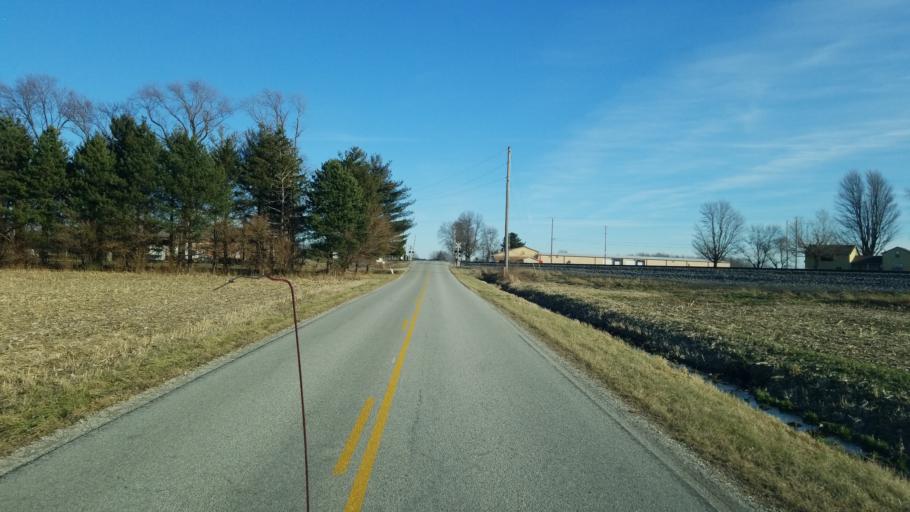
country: US
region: Ohio
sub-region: Sandusky County
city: Green Springs
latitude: 41.2560
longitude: -83.0149
